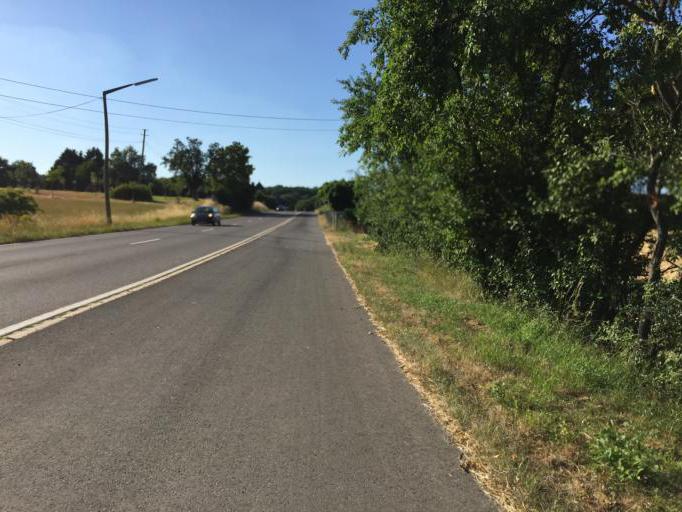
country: DE
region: Rheinland-Pfalz
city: Wallmerod
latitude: 50.4892
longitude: 7.9472
